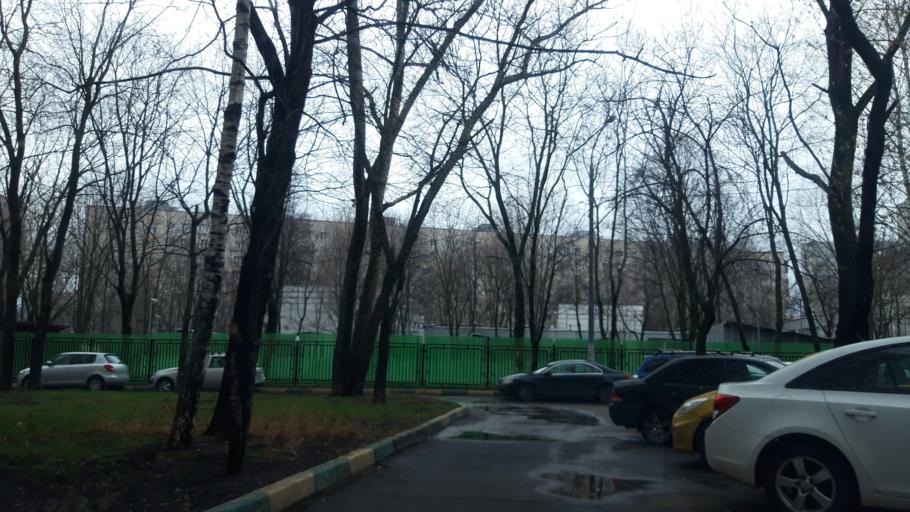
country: RU
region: Moscow
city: Likhobory
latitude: 55.8313
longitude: 37.5702
